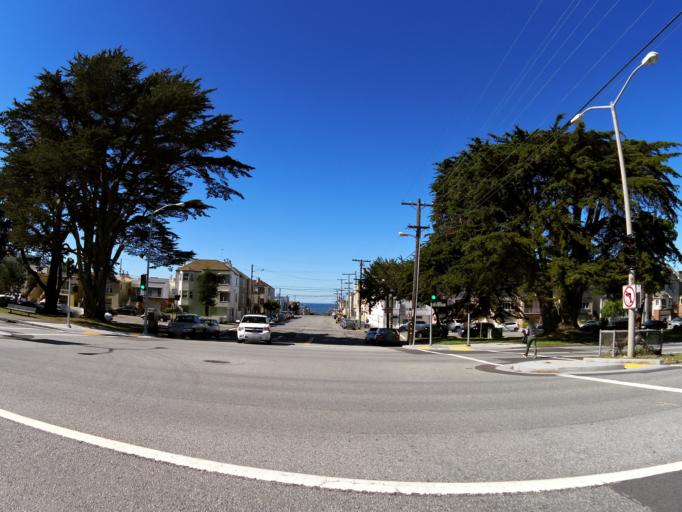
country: US
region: California
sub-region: San Mateo County
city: Daly City
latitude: 37.7628
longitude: -122.4957
